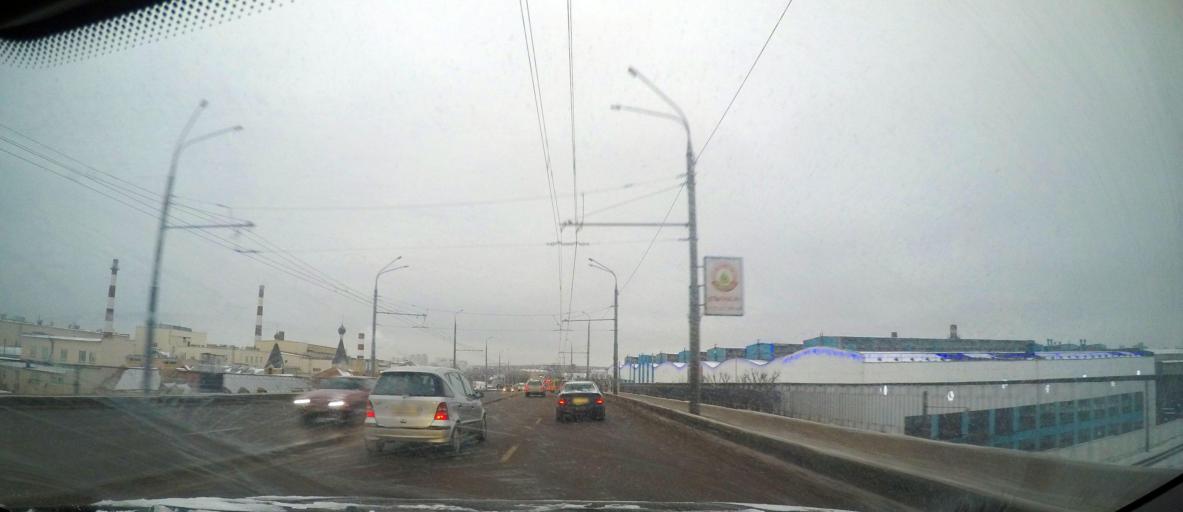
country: BY
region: Grodnenskaya
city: Hrodna
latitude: 53.6641
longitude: 23.8293
